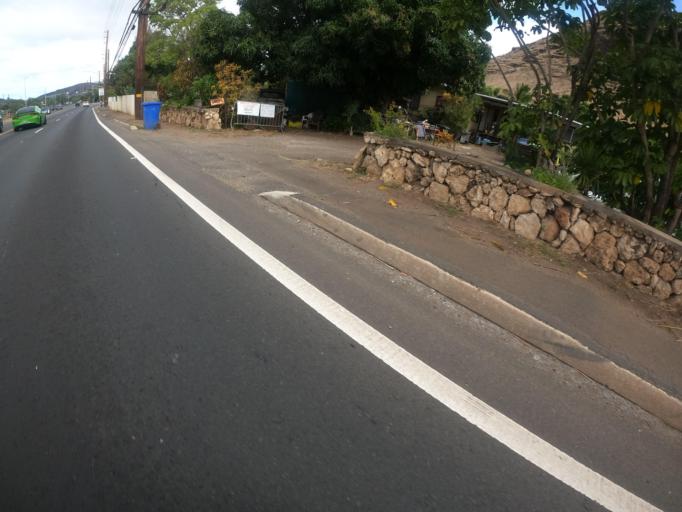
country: US
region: Hawaii
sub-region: Honolulu County
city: Nanakuli
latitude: 21.3714
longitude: -158.1370
